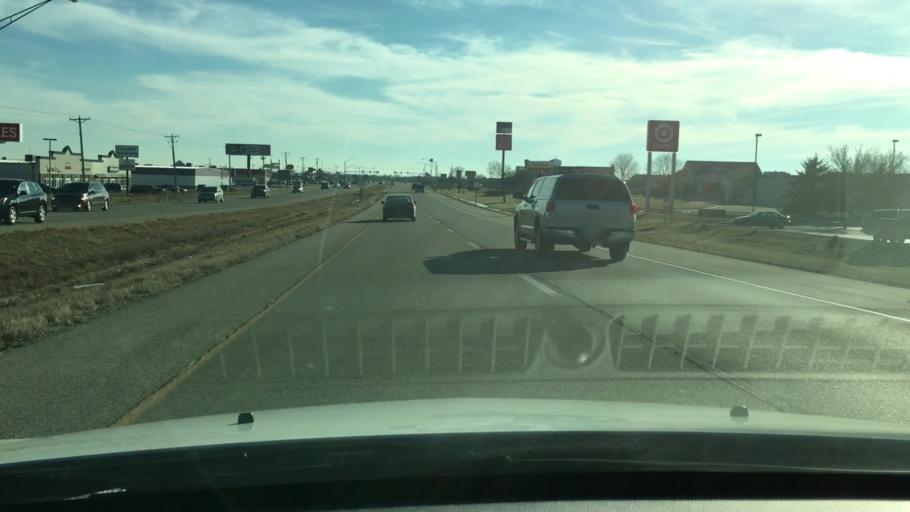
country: US
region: Illinois
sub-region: LaSalle County
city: Peru
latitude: 41.3629
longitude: -89.1257
